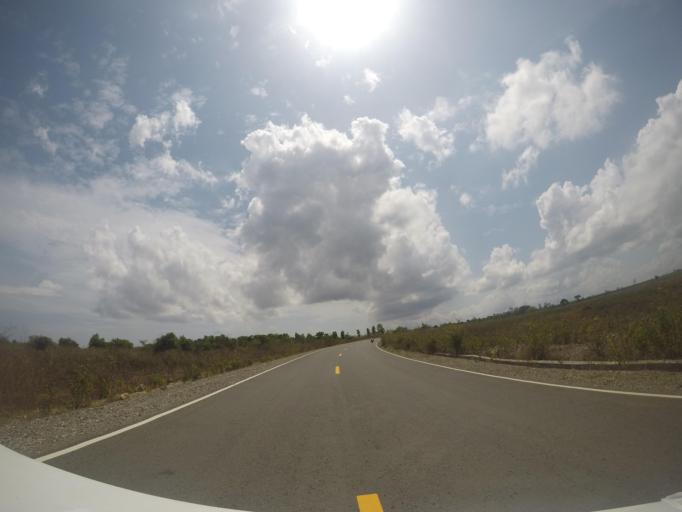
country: TL
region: Baucau
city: Baucau
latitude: -8.4742
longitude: 126.3931
